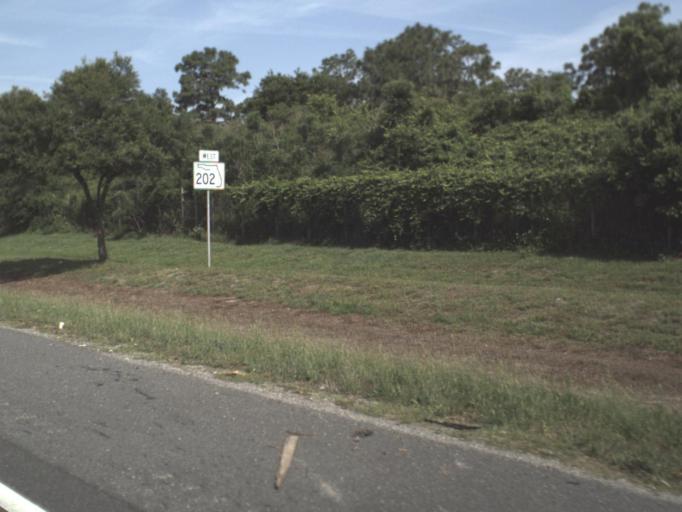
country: US
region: Florida
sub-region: Saint Johns County
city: Ponte Vedra Beach
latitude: 30.2515
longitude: -81.4750
